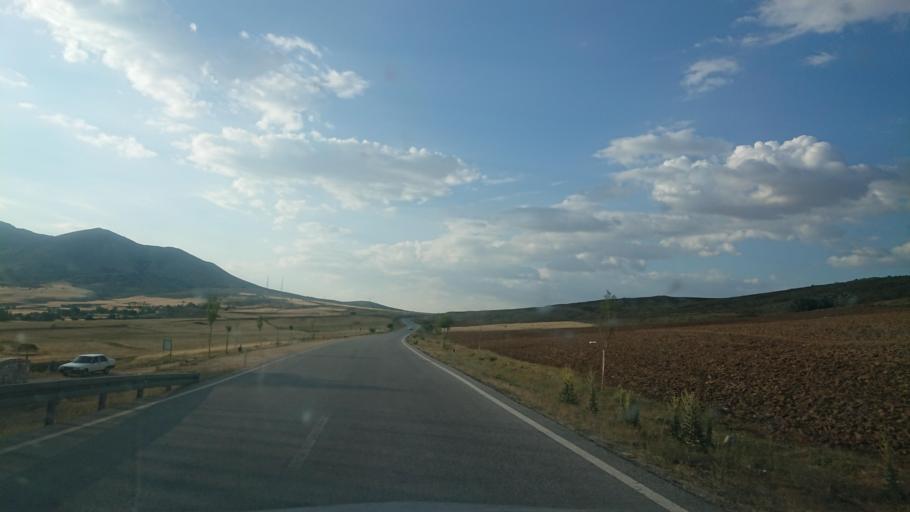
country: TR
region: Aksaray
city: Balci
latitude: 38.6014
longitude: 34.1034
